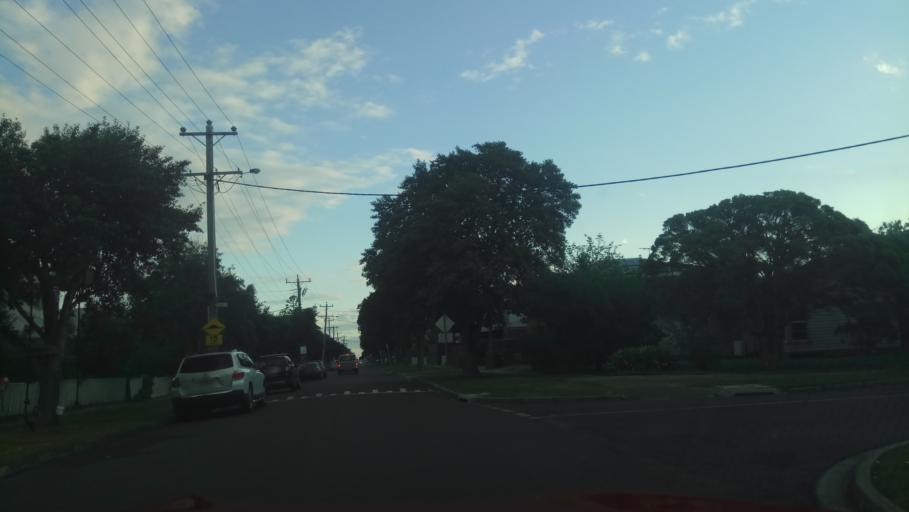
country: AU
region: Victoria
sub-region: Hobsons Bay
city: Williamstown North
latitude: -37.8611
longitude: 144.8864
